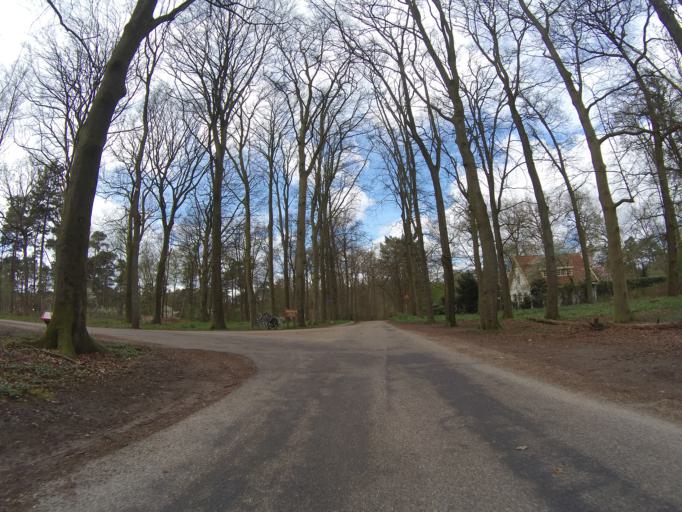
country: NL
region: North Holland
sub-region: Gemeente Hilversum
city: Hilversum
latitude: 52.1992
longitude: 5.2151
